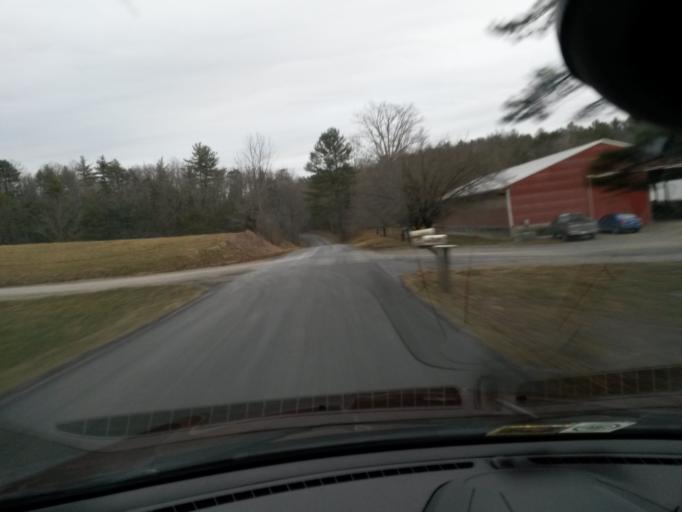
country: US
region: Virginia
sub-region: Bath County
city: Warm Springs
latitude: 38.0368
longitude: -79.6968
